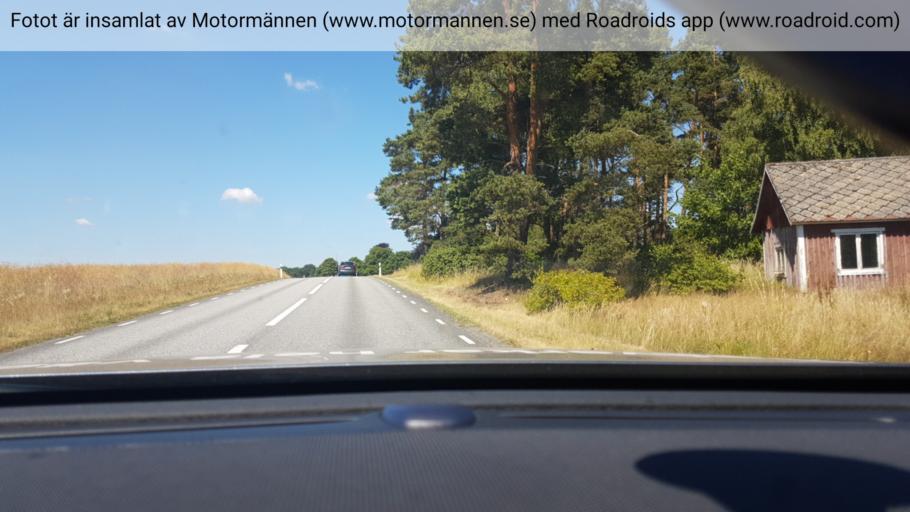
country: SE
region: Skane
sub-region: Hassleholms Kommun
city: Hassleholm
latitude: 56.1820
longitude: 13.8557
